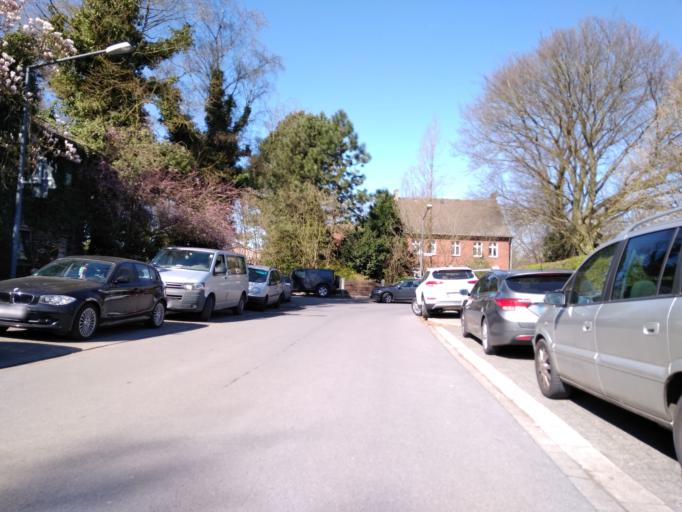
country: DE
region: North Rhine-Westphalia
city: Herten
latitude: 51.6130
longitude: 7.1117
